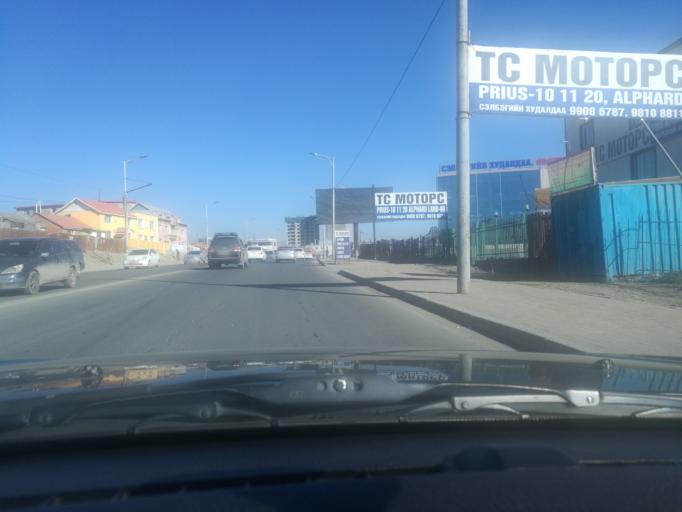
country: MN
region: Ulaanbaatar
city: Ulaanbaatar
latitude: 47.9308
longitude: 106.9050
